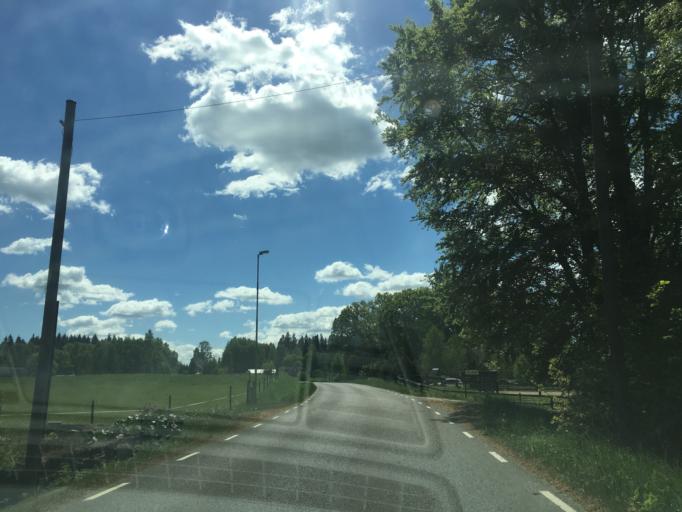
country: SE
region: Blekinge
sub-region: Olofstroms Kommun
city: Olofstroem
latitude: 56.3980
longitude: 14.5830
